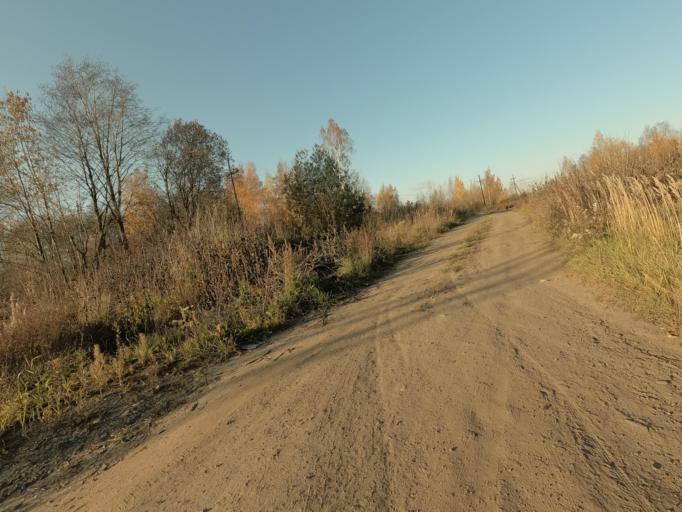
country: RU
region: Leningrad
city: Kirovsk
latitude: 59.8635
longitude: 31.0100
